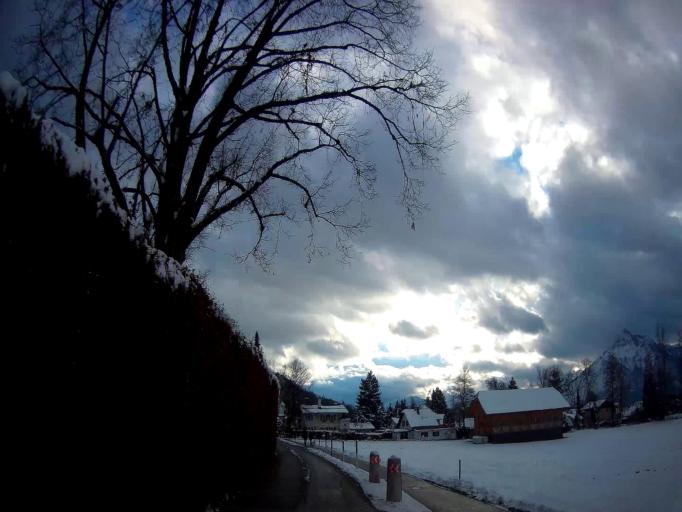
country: AT
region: Salzburg
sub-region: Politischer Bezirk Salzburg-Umgebung
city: Elsbethen
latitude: 47.7803
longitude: 13.0890
